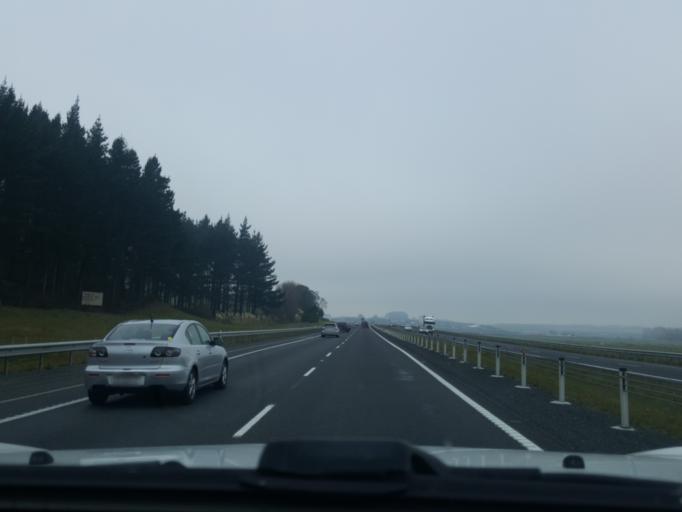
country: NZ
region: Waikato
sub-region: Waikato District
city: Te Kauwhata
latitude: -37.3419
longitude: 175.0662
